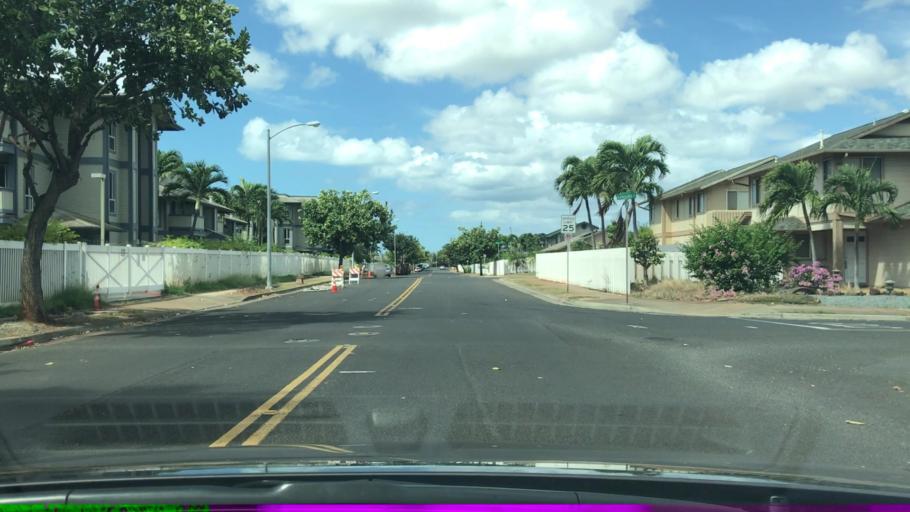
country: US
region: Hawaii
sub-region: Honolulu County
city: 'Ewa Gentry
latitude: 21.3354
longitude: -158.0255
